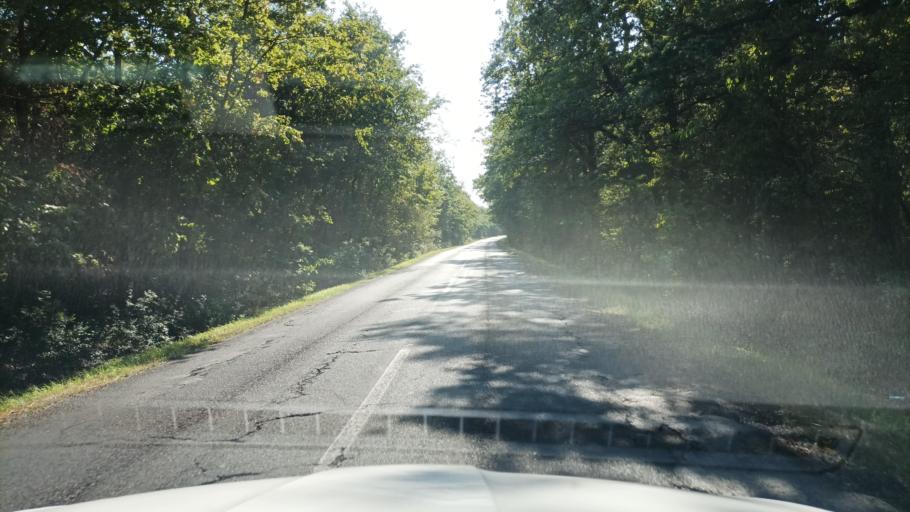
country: HU
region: Pest
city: Isaszeg
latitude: 47.5730
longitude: 19.4363
